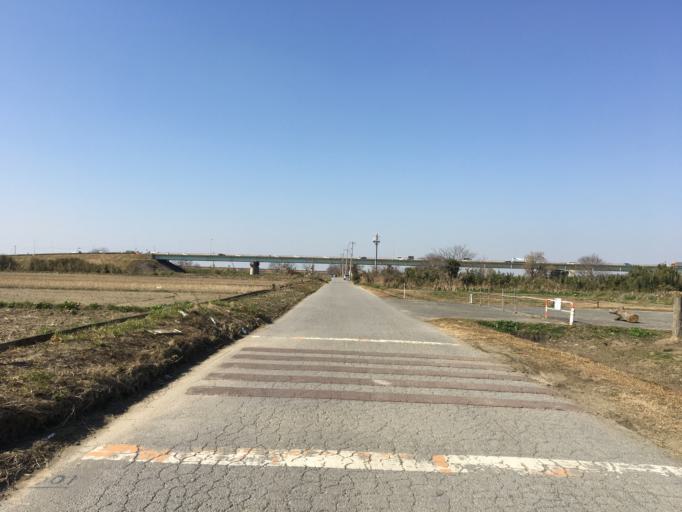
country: JP
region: Saitama
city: Shiki
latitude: 35.8520
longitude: 139.5903
